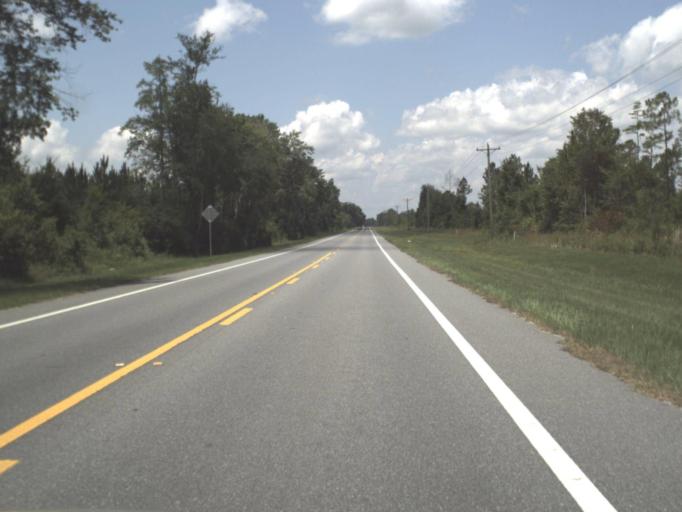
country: US
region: Florida
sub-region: Union County
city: Lake Butler
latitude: 30.0069
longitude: -82.4807
